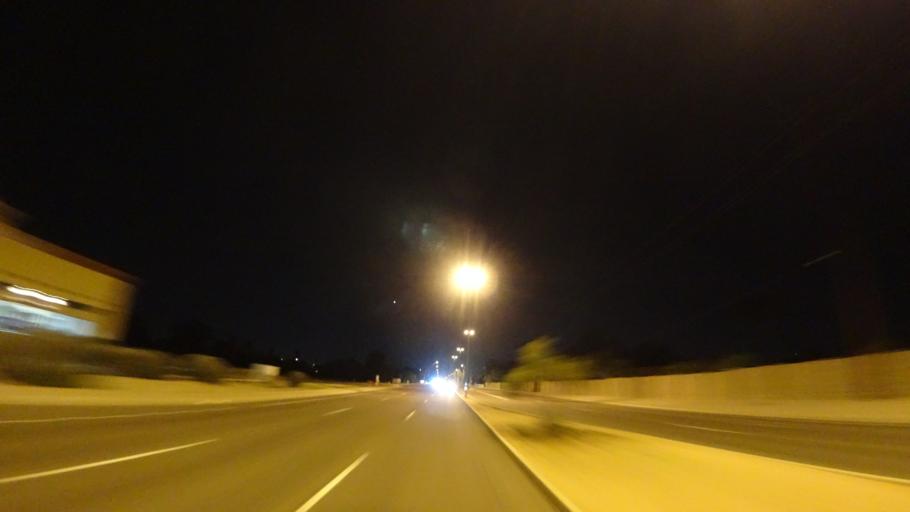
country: US
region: Arizona
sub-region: Maricopa County
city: Gilbert
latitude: 33.3939
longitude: -111.7033
